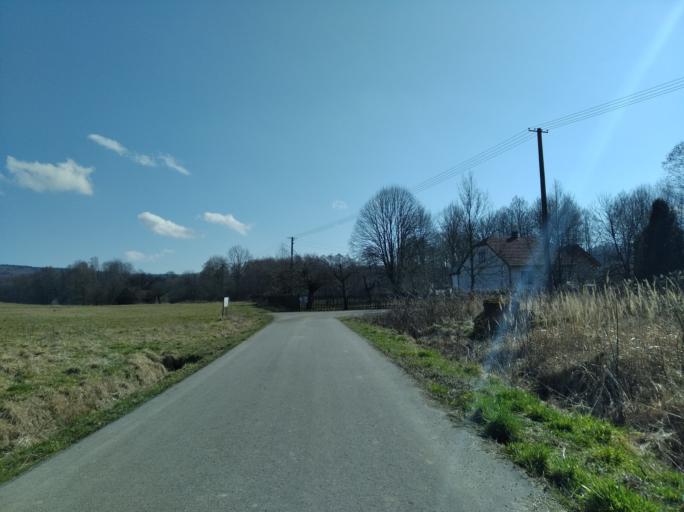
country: PL
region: Subcarpathian Voivodeship
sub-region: Powiat strzyzowski
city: Wysoka Strzyzowska
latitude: 49.8279
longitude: 21.7448
